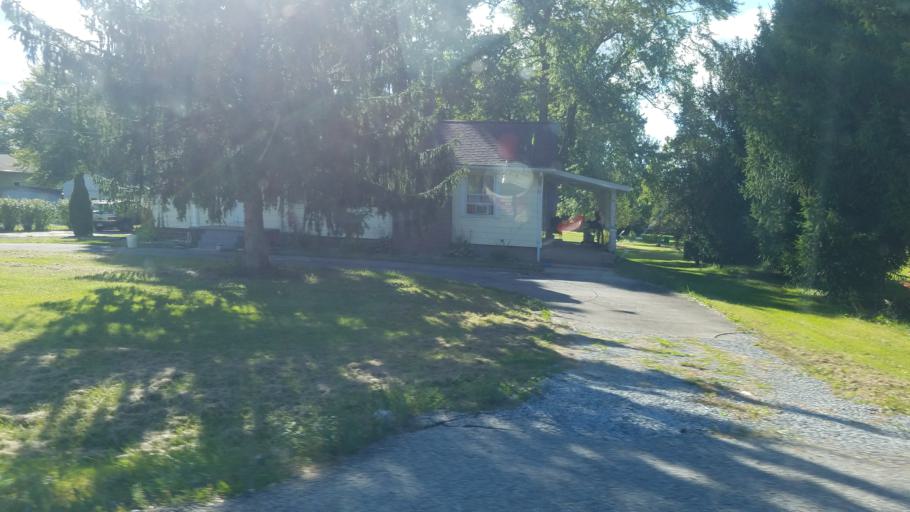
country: US
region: Ohio
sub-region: Mahoning County
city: Austintown
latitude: 41.0736
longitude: -80.7625
